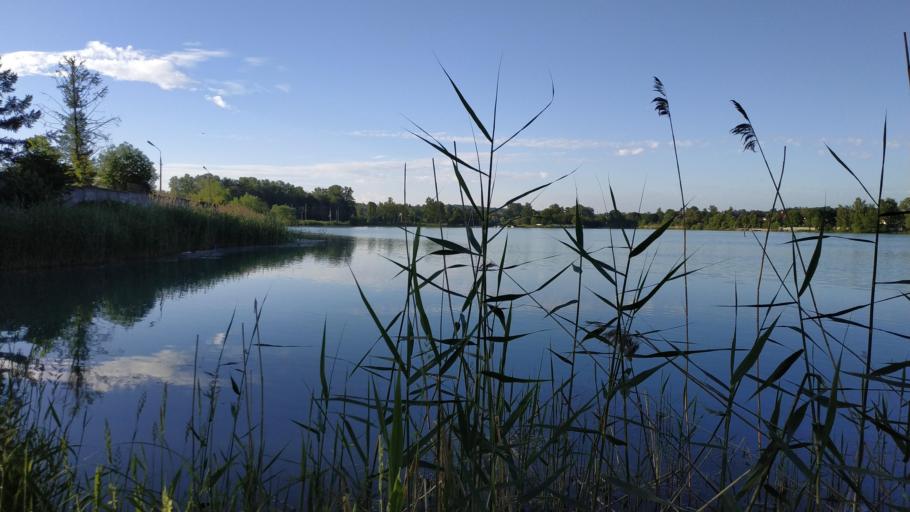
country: RU
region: St.-Petersburg
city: Krasnoye Selo
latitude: 59.7273
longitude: 30.1008
